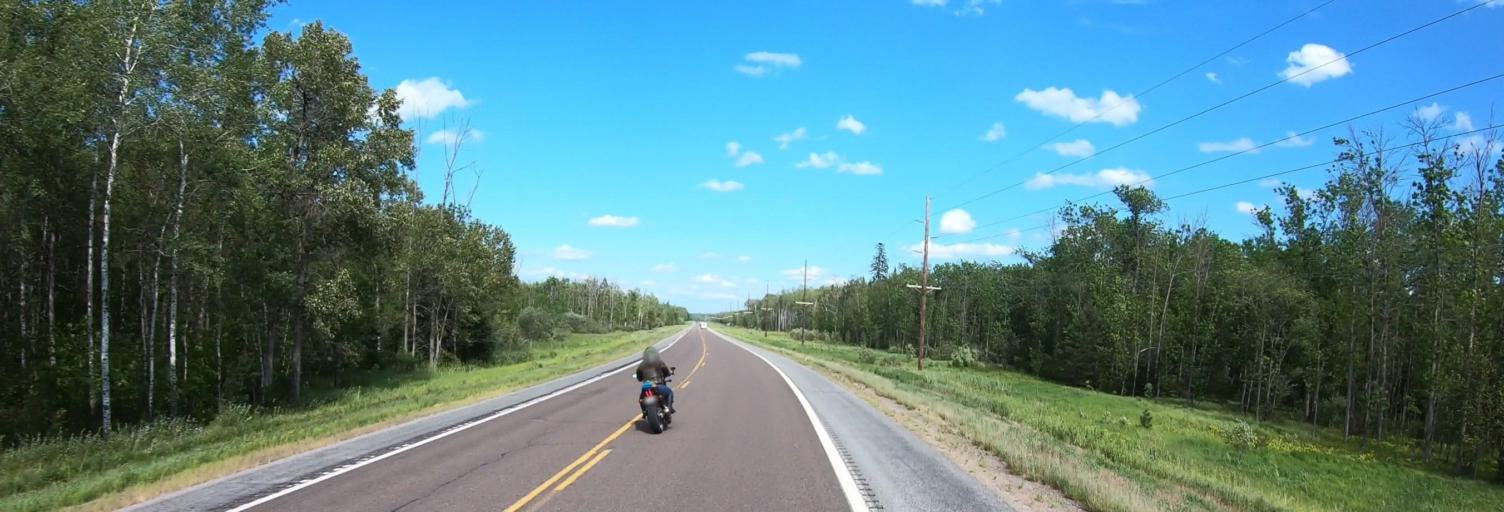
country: US
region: Minnesota
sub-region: Saint Louis County
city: Parkville
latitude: 47.8467
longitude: -92.5125
